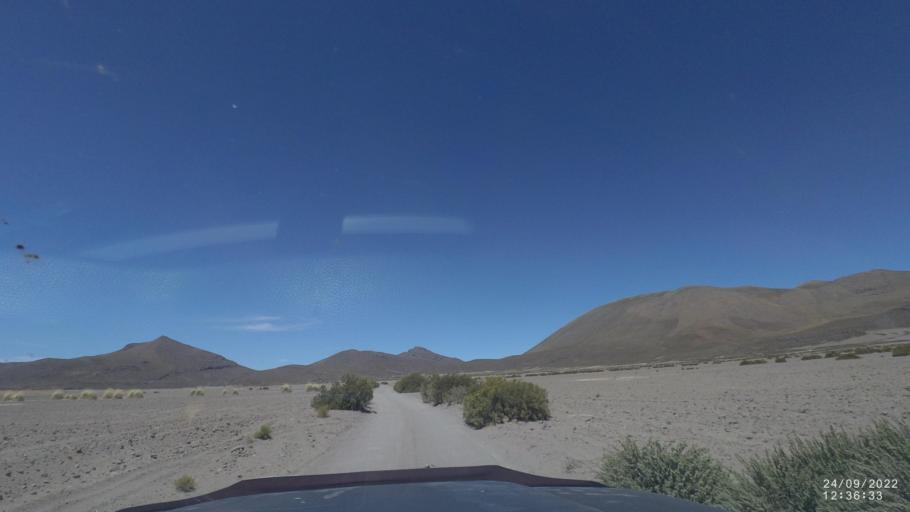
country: BO
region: Potosi
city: Colchani
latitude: -19.7871
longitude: -67.5880
